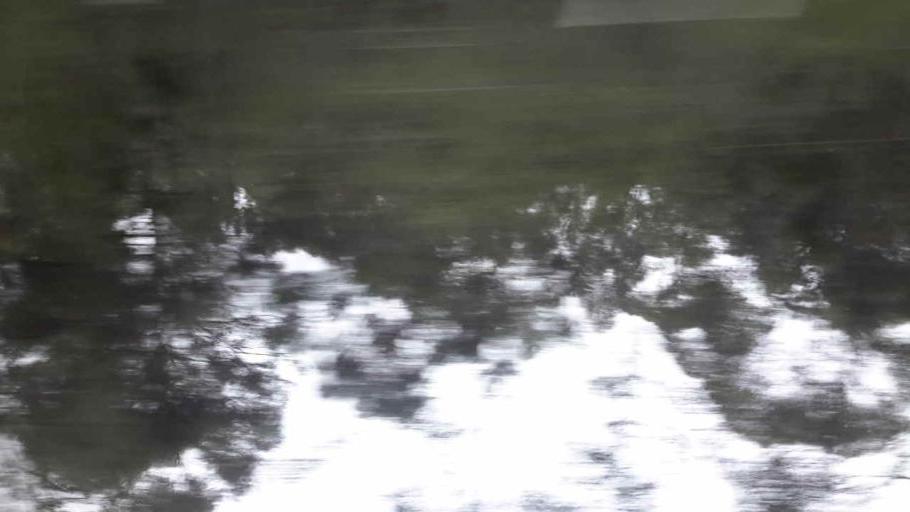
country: AU
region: New South Wales
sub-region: Penrith Municipality
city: Werrington Downs
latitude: -33.6959
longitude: 150.7275
